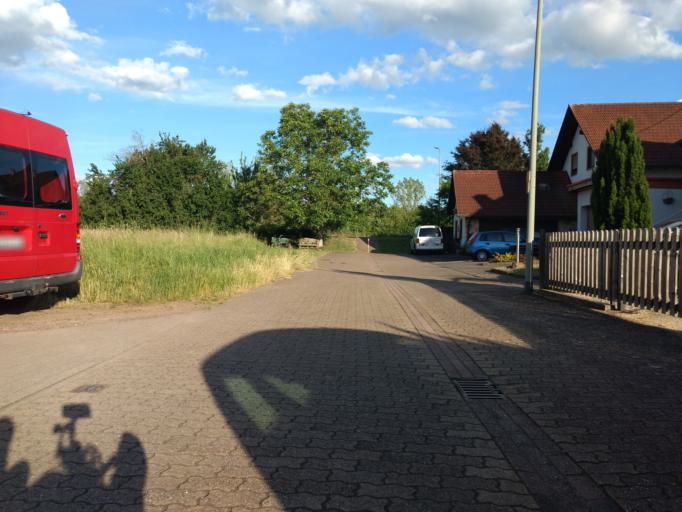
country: DE
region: Saarland
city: Rehlingen-Siersburg
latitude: 49.3779
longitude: 6.6922
